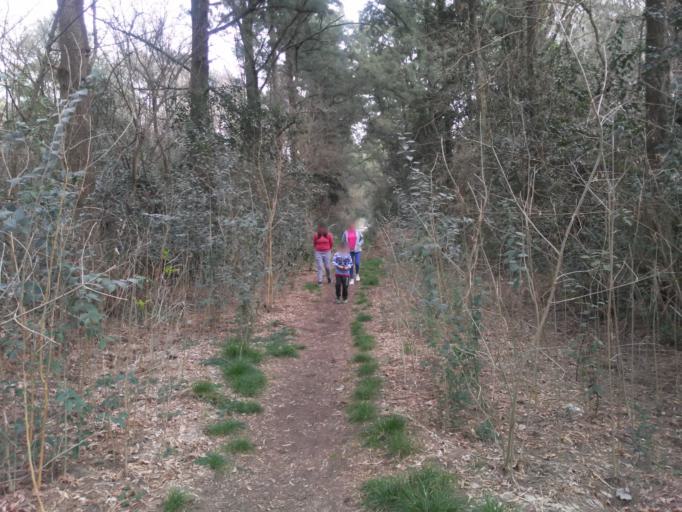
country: AR
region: Buenos Aires
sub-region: Partido de General Rodriguez
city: General Rodriguez
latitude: -34.6631
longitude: -58.8575
